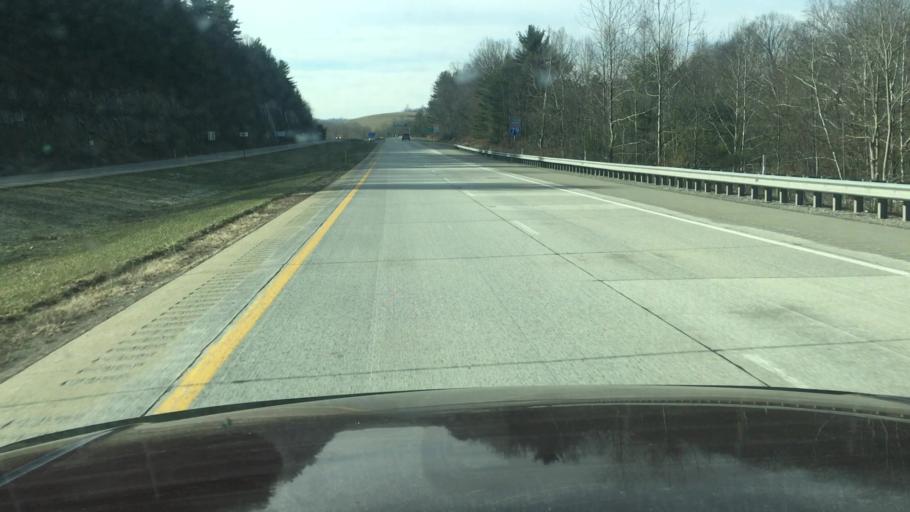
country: US
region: West Virginia
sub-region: Monongalia County
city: Star City
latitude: 39.7250
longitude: -80.0606
